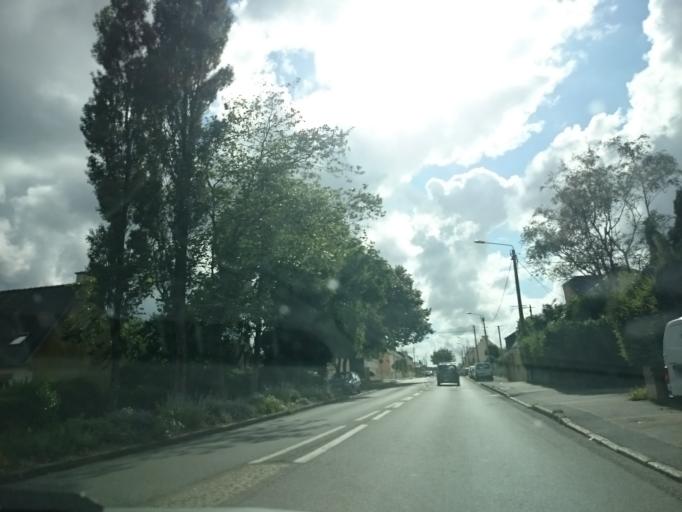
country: FR
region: Brittany
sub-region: Departement du Finistere
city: Brest
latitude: 48.4137
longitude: -4.4461
